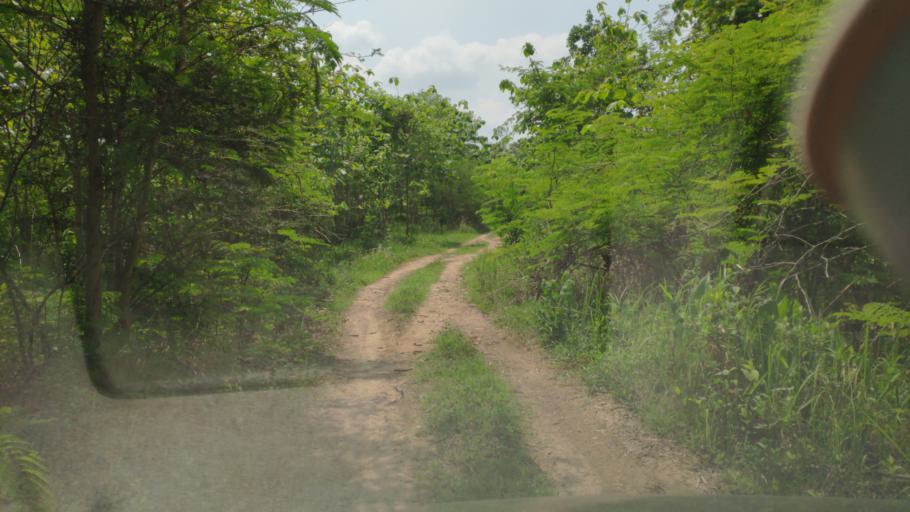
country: ID
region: Central Java
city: Gaplokan
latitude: -6.9141
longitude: 111.2664
